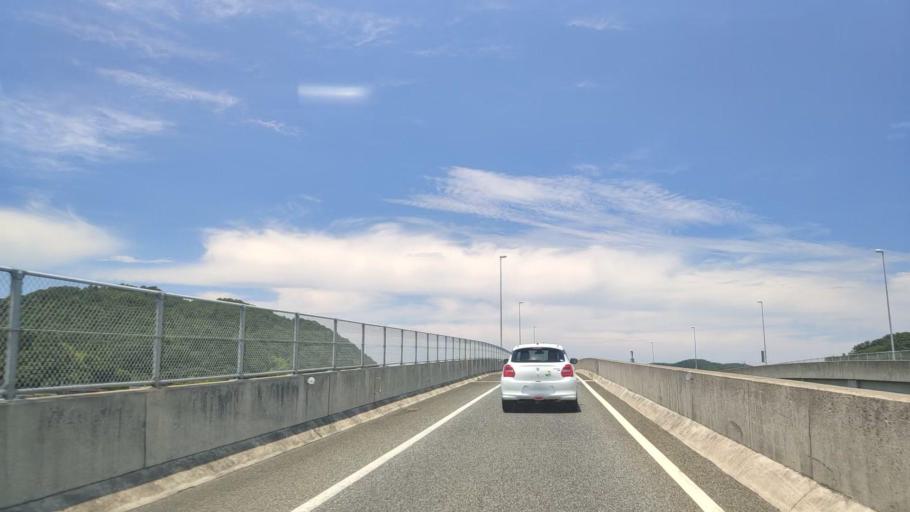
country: JP
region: Tottori
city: Tottori
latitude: 35.4642
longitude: 134.2430
